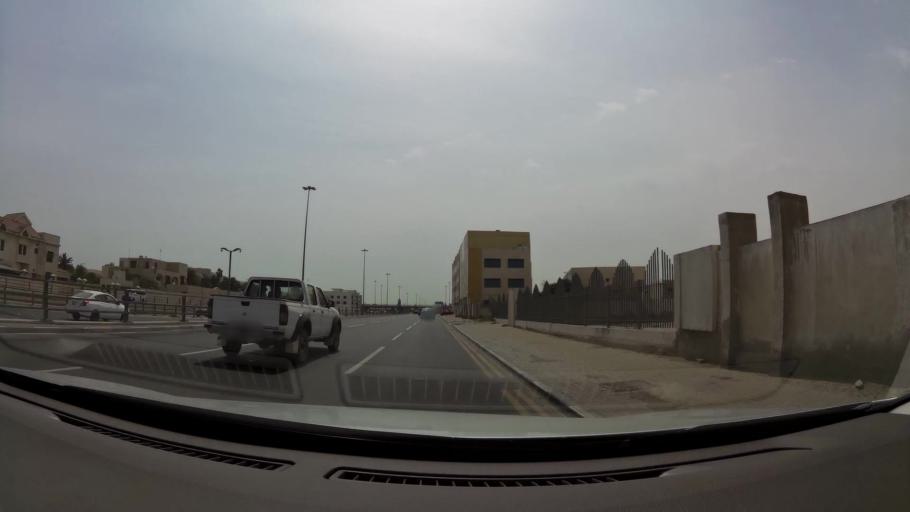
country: QA
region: Baladiyat ad Dawhah
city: Doha
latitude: 25.2673
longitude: 51.4946
